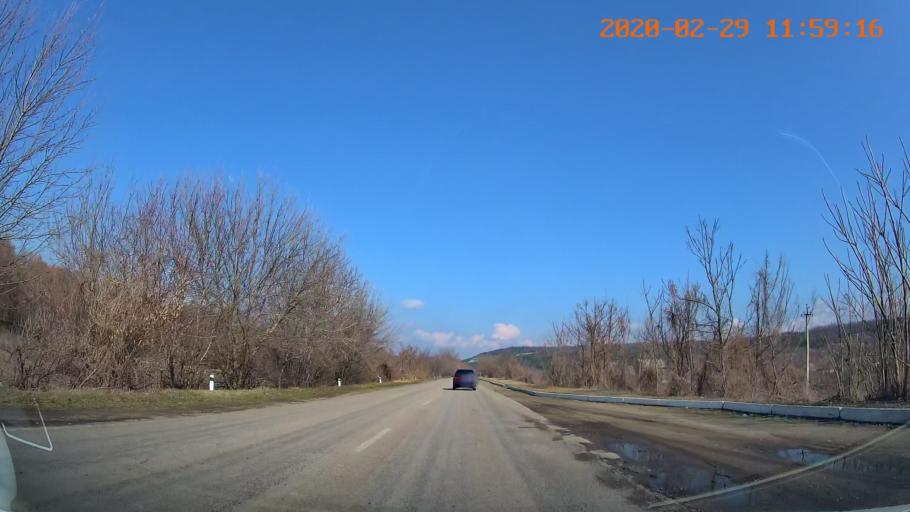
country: MD
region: Telenesti
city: Ribnita
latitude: 47.8232
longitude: 29.0161
